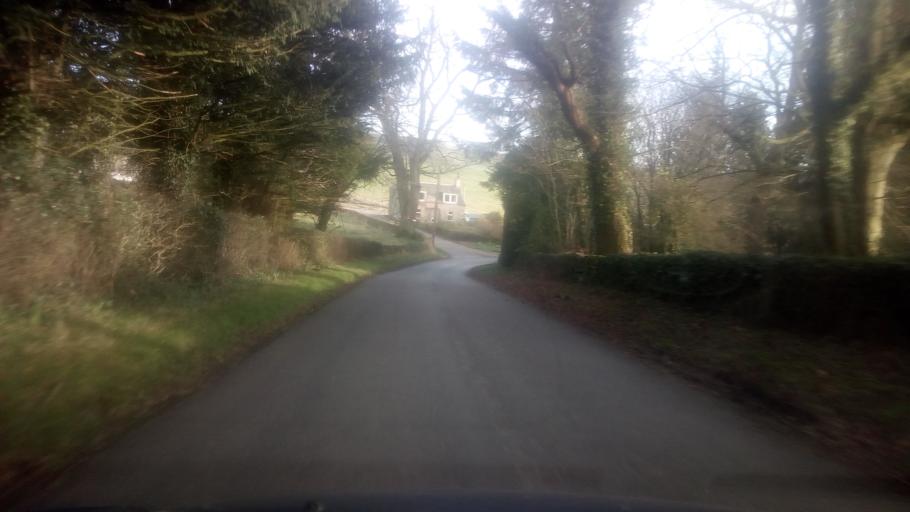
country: GB
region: Scotland
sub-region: The Scottish Borders
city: Jedburgh
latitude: 55.4552
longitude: -2.6335
